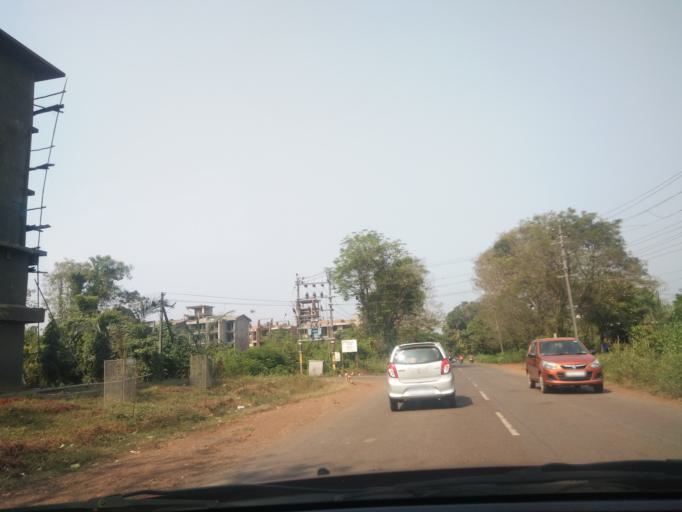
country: IN
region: Goa
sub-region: North Goa
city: Sanquelim
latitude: 15.5552
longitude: 74.0262
